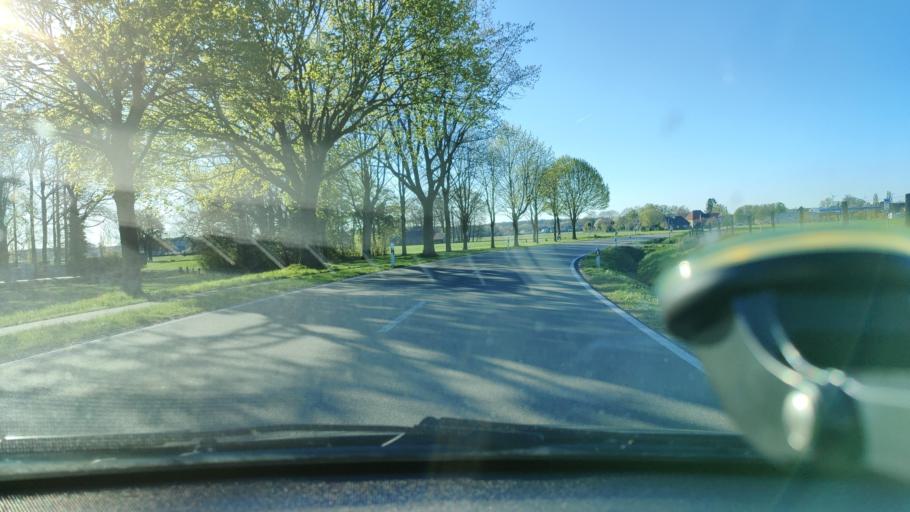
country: DE
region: North Rhine-Westphalia
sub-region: Regierungsbezirk Munster
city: Legden
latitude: 52.0240
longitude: 7.1072
